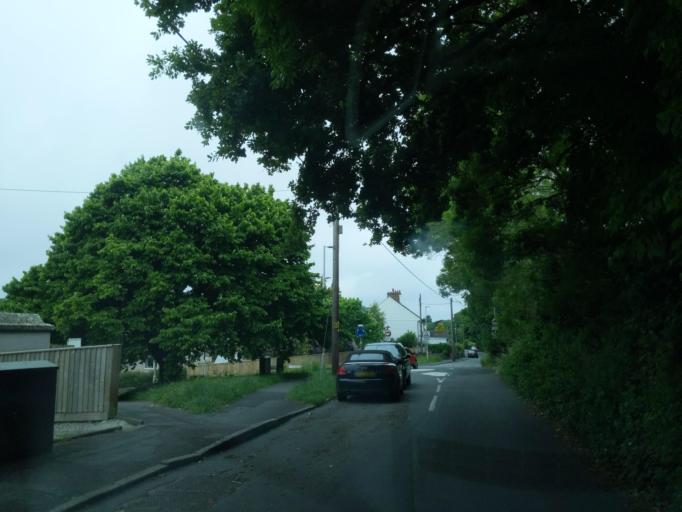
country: GB
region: England
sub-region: Devon
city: Plympton
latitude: 50.3837
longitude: -4.0420
